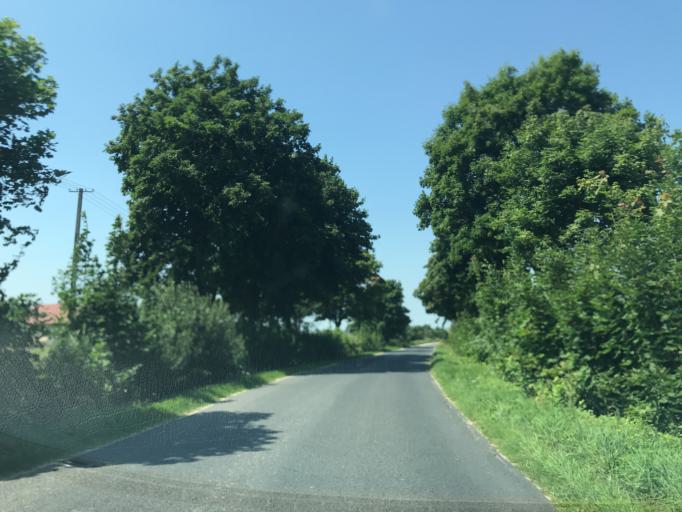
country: PL
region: Kujawsko-Pomorskie
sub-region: Powiat lipnowski
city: Chrostkowo
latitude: 52.9959
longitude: 19.2233
